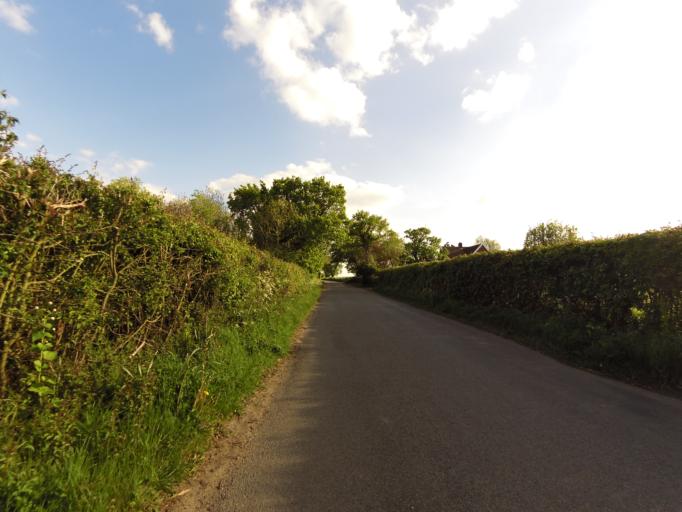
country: GB
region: England
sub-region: Suffolk
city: Beccles
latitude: 52.3999
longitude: 1.5398
